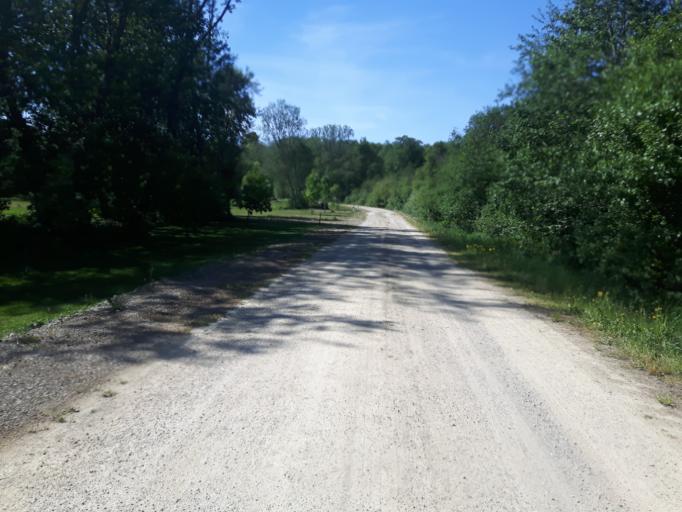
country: EE
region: Ida-Virumaa
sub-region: Kivioli linn
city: Kivioli
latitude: 59.4338
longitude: 26.9536
